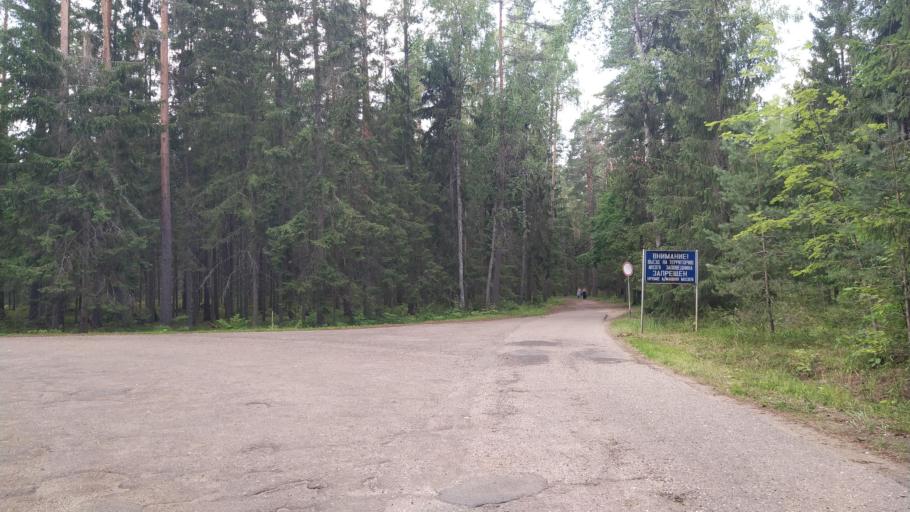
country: RU
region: Pskov
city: Pushkinskiye Gory
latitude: 57.0583
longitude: 28.9402
